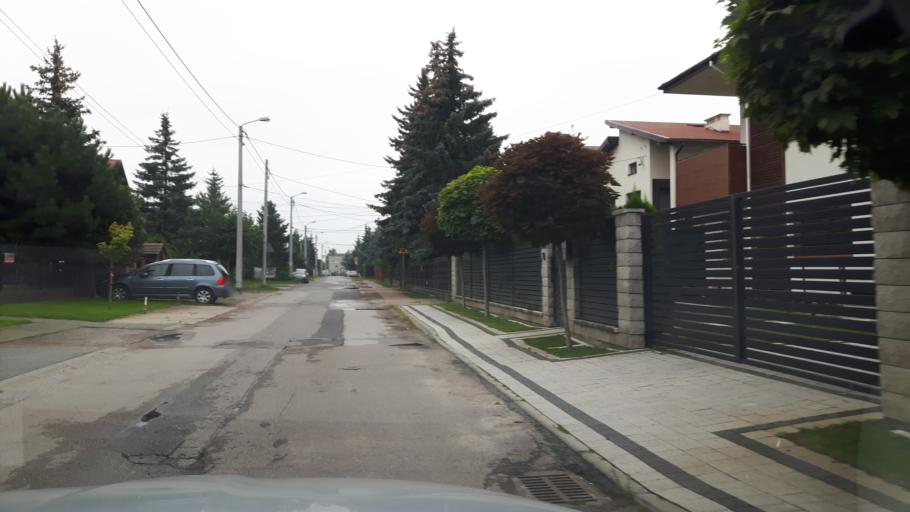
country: PL
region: Masovian Voivodeship
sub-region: Powiat wolominski
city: Marki
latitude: 52.3184
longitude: 21.1078
